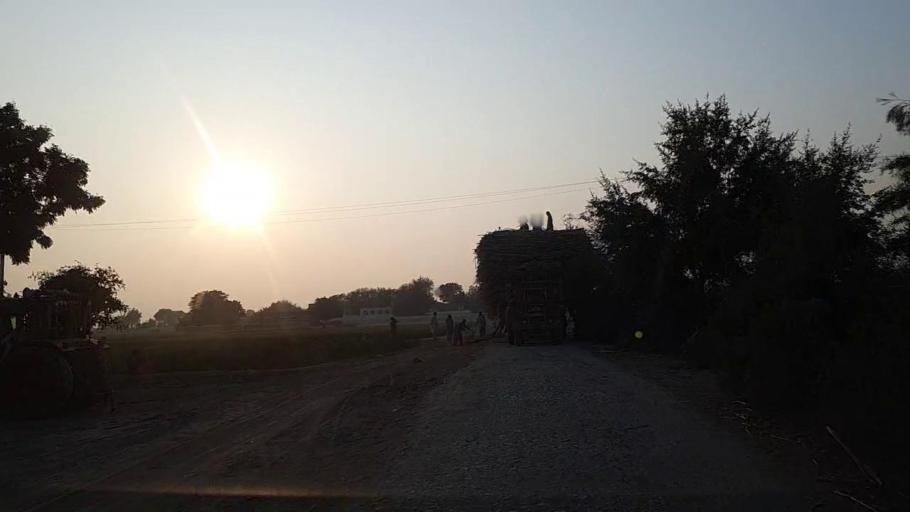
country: PK
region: Sindh
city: Sann
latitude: 26.1947
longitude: 68.0834
